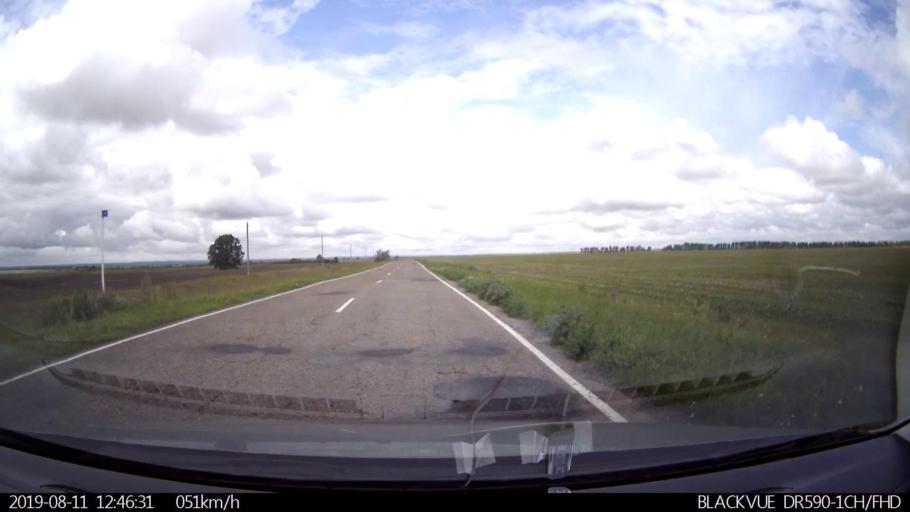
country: RU
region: Ulyanovsk
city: Ignatovka
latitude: 53.8647
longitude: 47.7180
